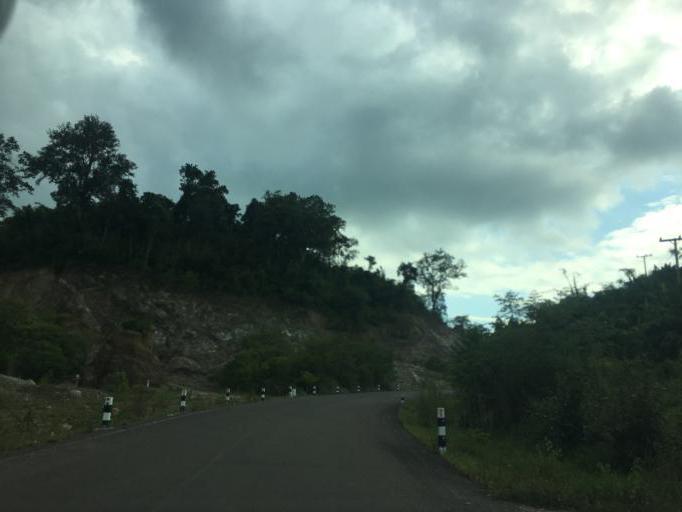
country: TH
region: Nong Khai
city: Sangkhom
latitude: 18.1948
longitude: 102.2216
